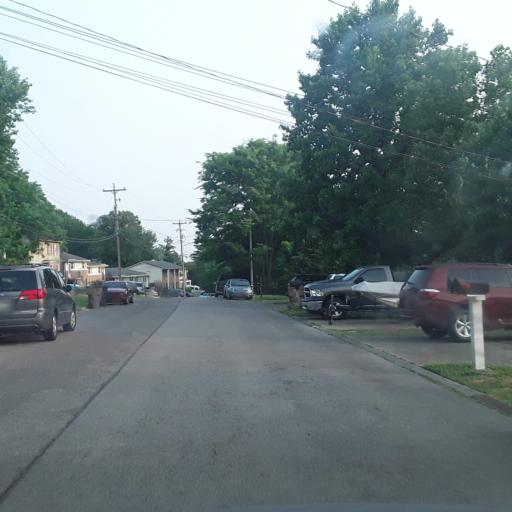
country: US
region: Tennessee
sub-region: Williamson County
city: Brentwood Estates
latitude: 36.0504
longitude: -86.7255
